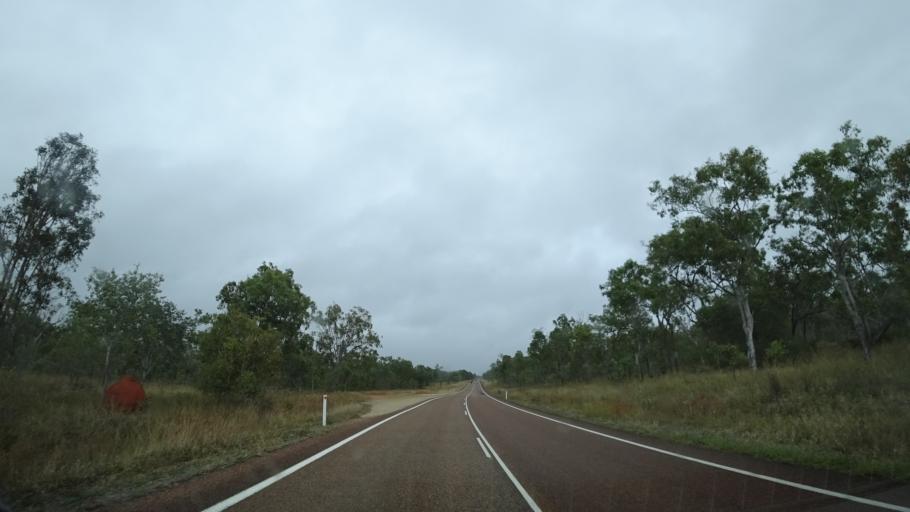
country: AU
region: Queensland
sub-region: Tablelands
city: Ravenshoe
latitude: -17.6837
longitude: 145.2321
